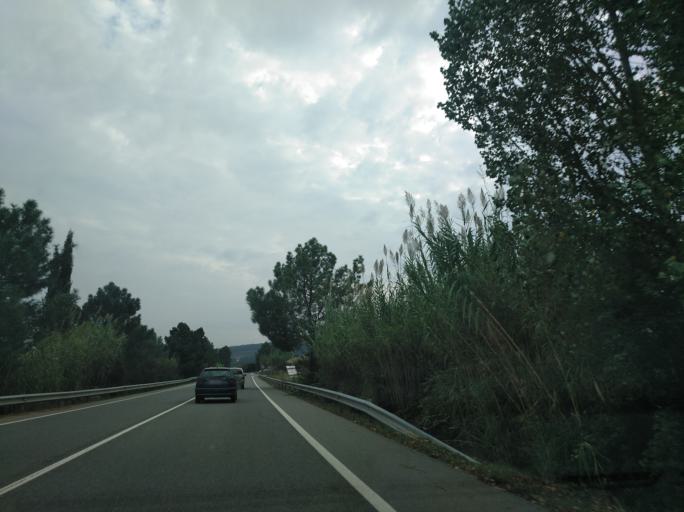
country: ES
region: Catalonia
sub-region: Provincia de Girona
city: Santa Coloma de Farners
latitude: 41.8683
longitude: 2.6646
